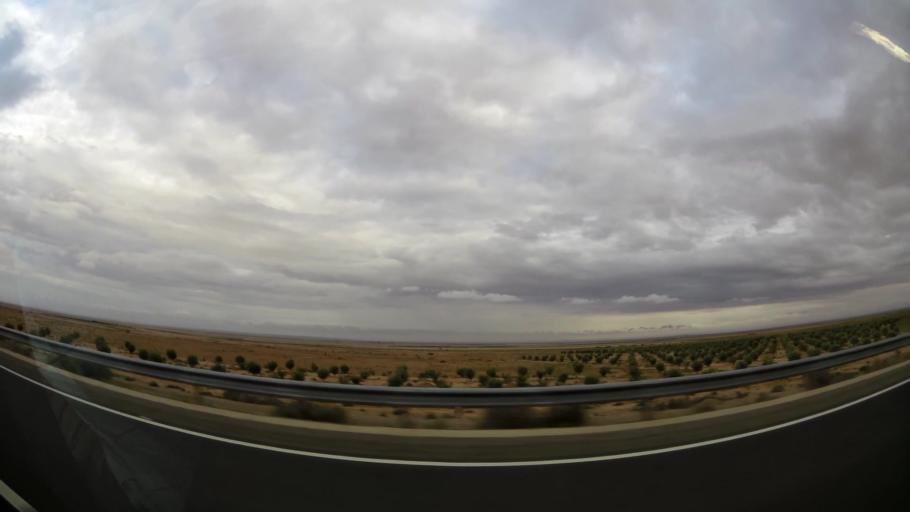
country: MA
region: Taza-Al Hoceima-Taounate
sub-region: Taza
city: Guercif
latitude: 34.3251
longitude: -3.5652
